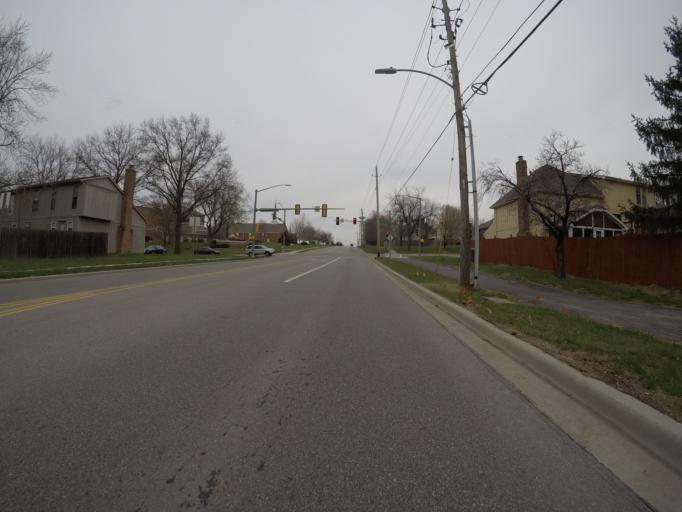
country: US
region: Kansas
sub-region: Johnson County
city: Olathe
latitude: 38.8691
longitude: -94.7861
